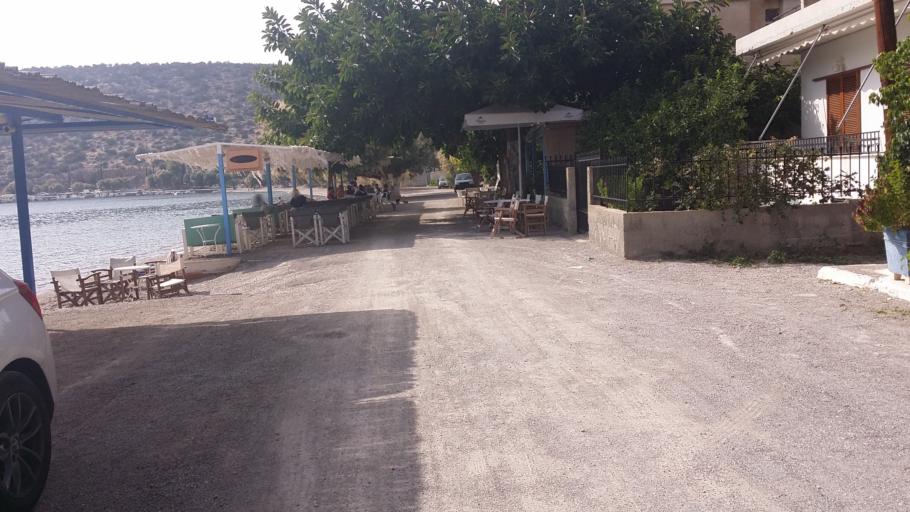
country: GR
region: Central Greece
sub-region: Nomos Voiotias
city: Korini
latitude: 38.2371
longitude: 22.8892
